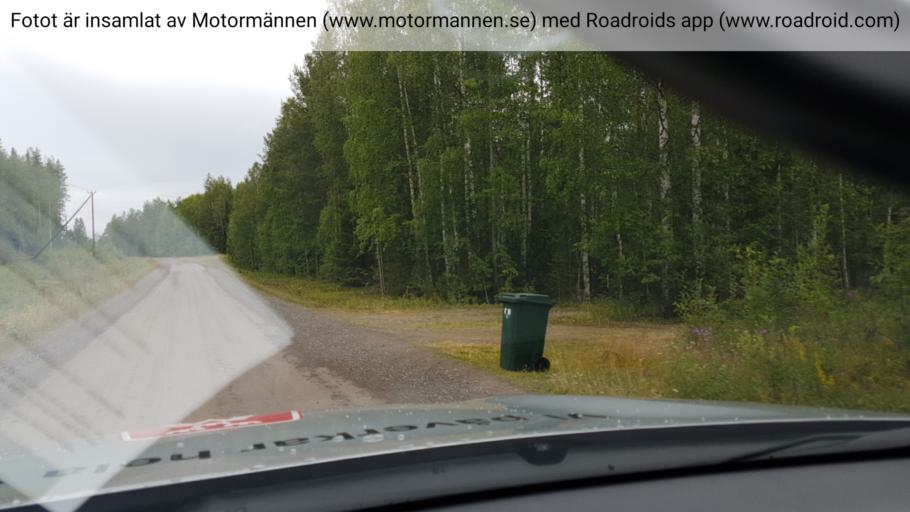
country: SE
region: Norrbotten
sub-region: Alvsbyns Kommun
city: AElvsbyn
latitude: 65.9996
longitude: 21.1600
